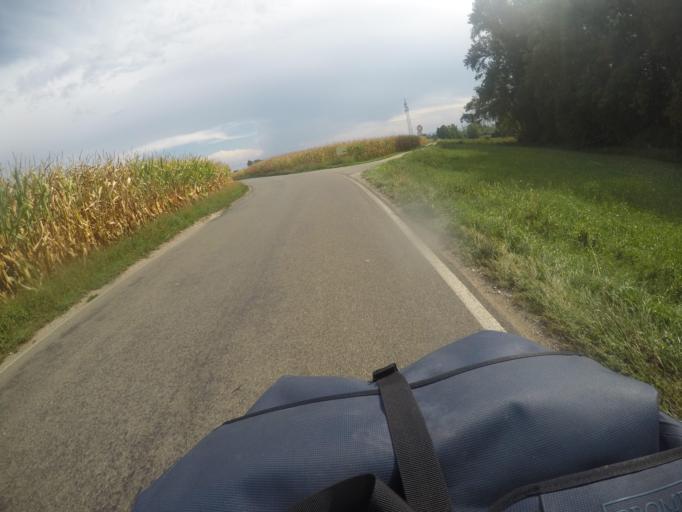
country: DE
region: Baden-Wuerttemberg
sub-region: Freiburg Region
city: Efringen-Kirchen
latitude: 47.6369
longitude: 7.5709
